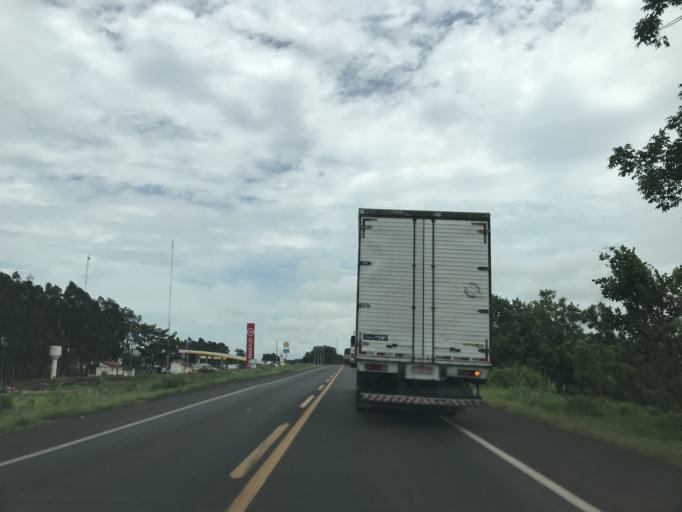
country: BR
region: Minas Gerais
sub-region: Frutal
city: Frutal
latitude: -19.8516
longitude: -48.9625
